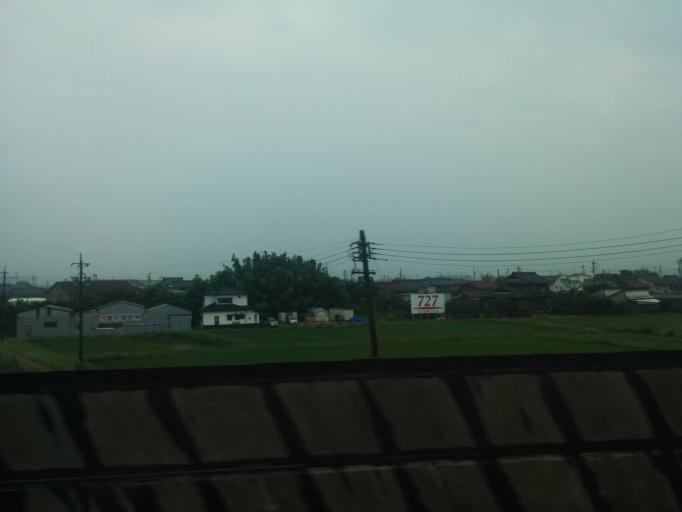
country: JP
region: Aichi
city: Inazawa
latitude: 35.2602
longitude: 136.7617
